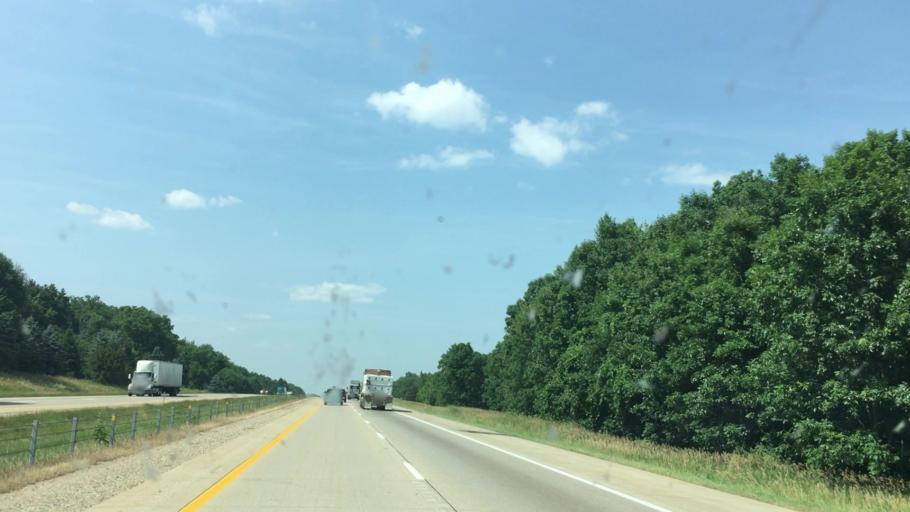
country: US
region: Michigan
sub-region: Allegan County
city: Otsego
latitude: 42.5022
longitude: -85.6532
